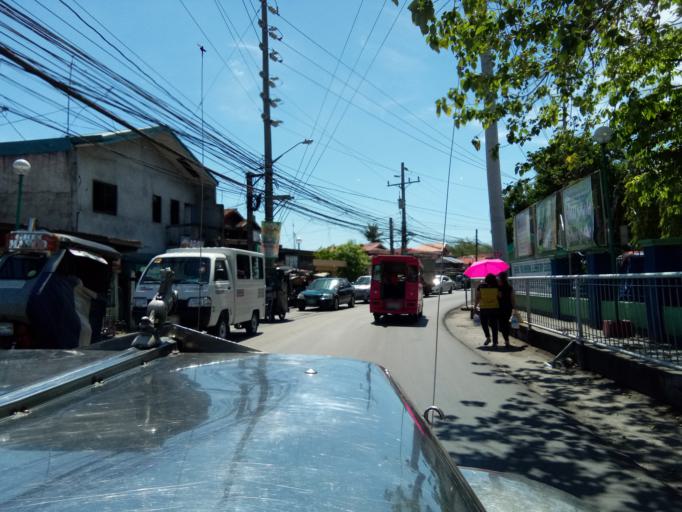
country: PH
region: Calabarzon
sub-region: Province of Cavite
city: General Trias
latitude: 14.3817
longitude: 120.8778
